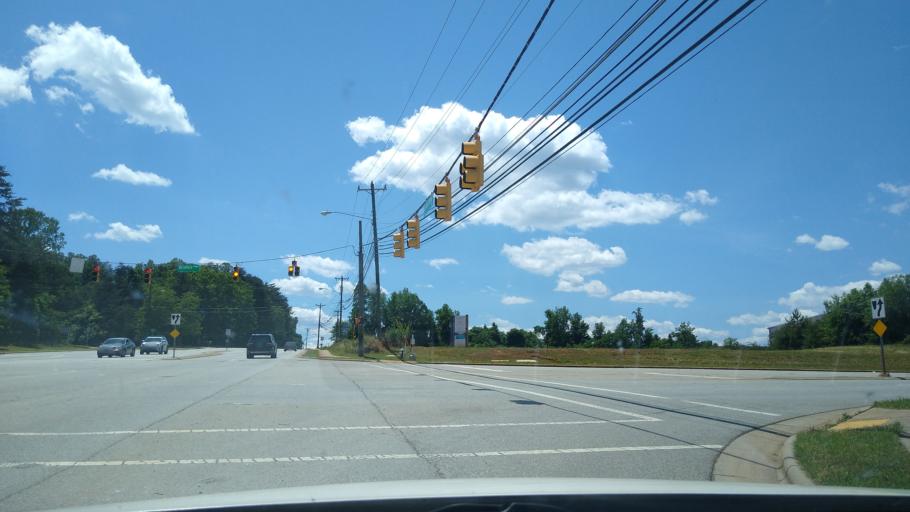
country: US
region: North Carolina
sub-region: Guilford County
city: Jamestown
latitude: 36.0665
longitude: -79.9045
